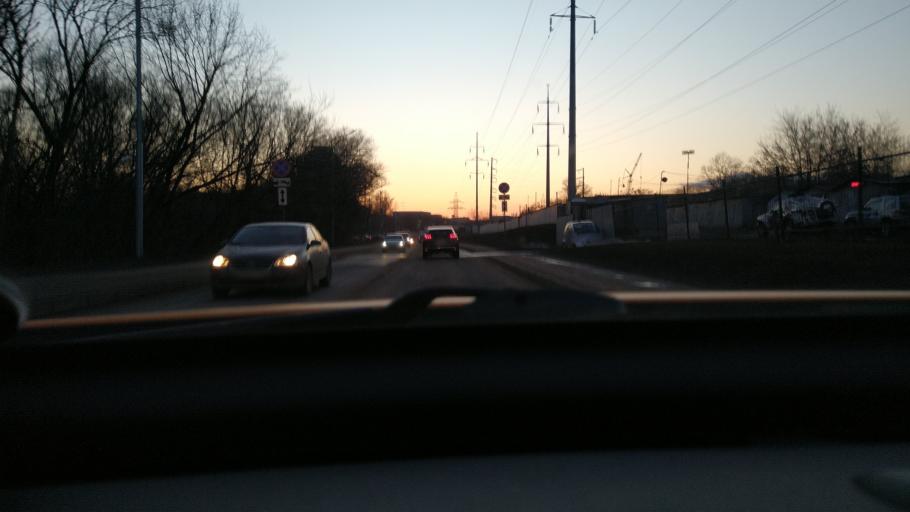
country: RU
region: Moscow
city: Strogino
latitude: 55.8372
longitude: 37.4173
